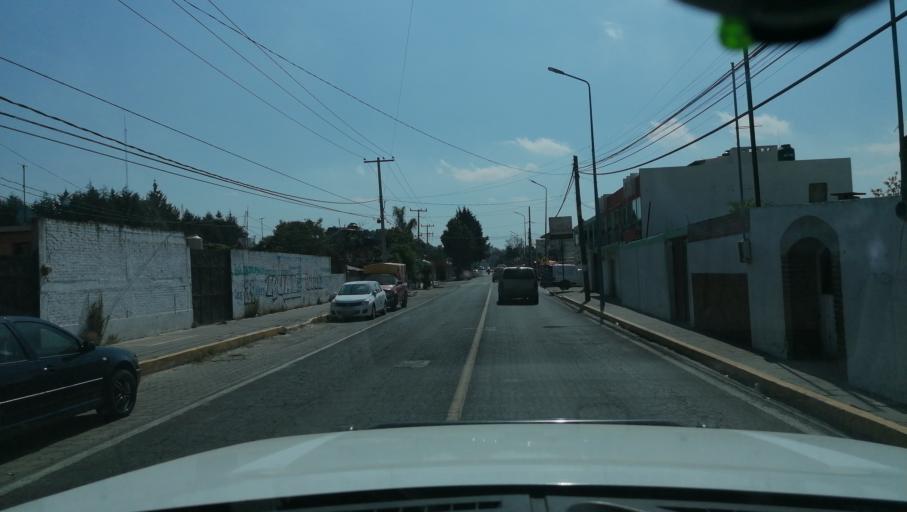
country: MX
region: Tlaxcala
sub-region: San Jeronimo Zacualpan
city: San Jeronimo Zacualpan
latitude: 19.2406
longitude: -98.2614
